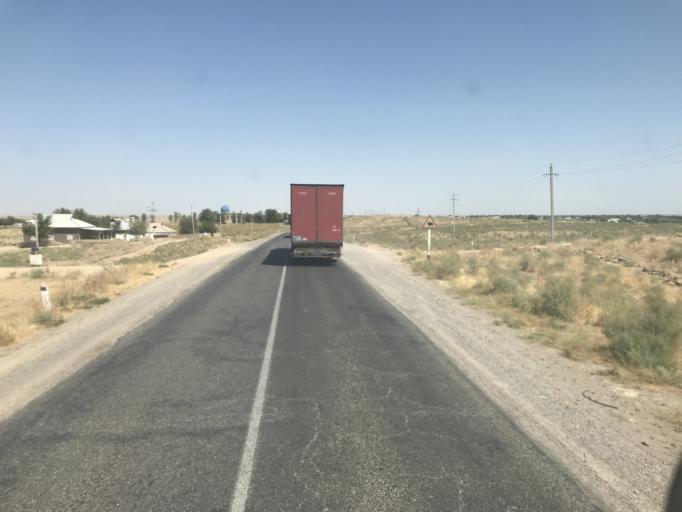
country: UZ
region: Toshkent
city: Chinoz
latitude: 41.3266
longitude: 68.6790
